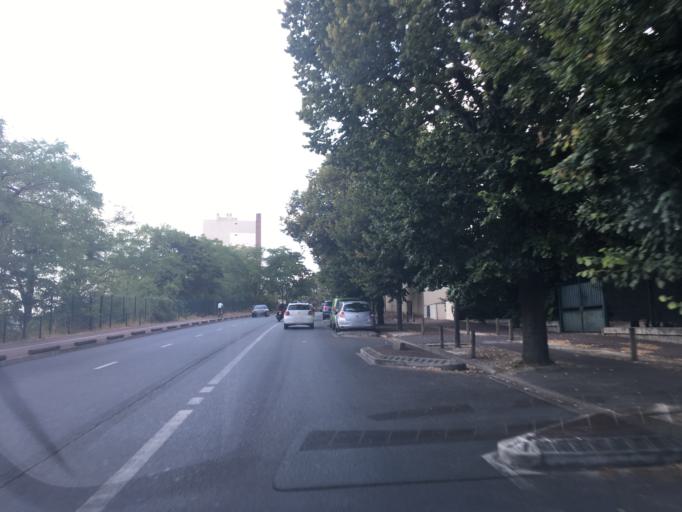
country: FR
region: Ile-de-France
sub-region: Departement du Val-de-Marne
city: Joinville-le-Pont
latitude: 48.8158
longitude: 2.4614
